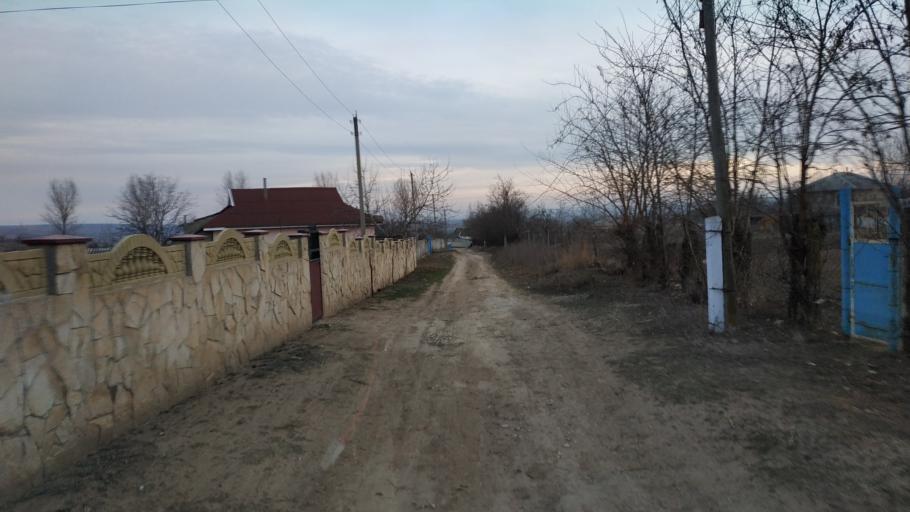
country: MD
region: Hincesti
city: Dancu
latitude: 46.7487
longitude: 28.2105
